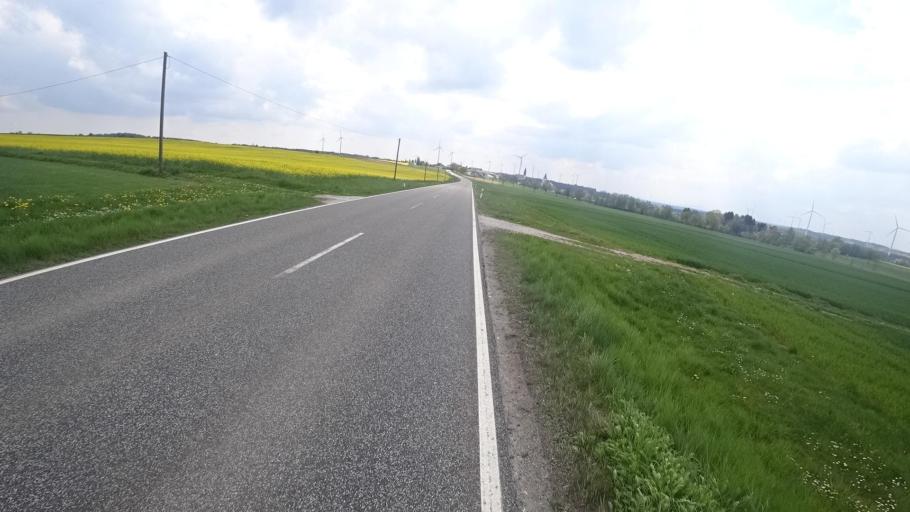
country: DE
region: Rheinland-Pfalz
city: Laubach
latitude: 50.0610
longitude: 7.5137
